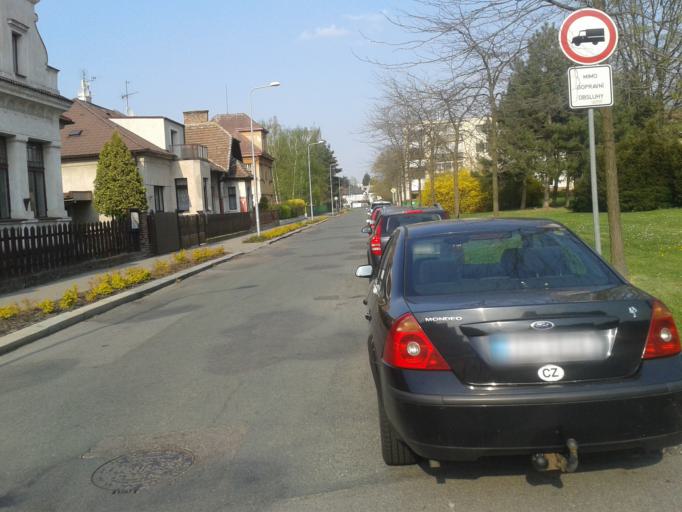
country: CZ
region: Pardubicky
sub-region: Okres Pardubice
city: Pardubice
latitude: 50.0371
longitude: 15.7894
